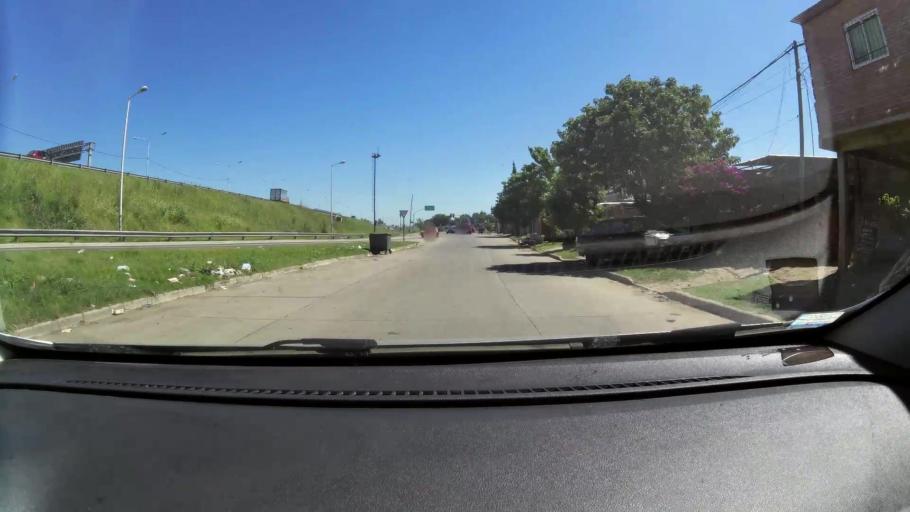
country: AR
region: Santa Fe
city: Perez
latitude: -32.9606
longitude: -60.7203
